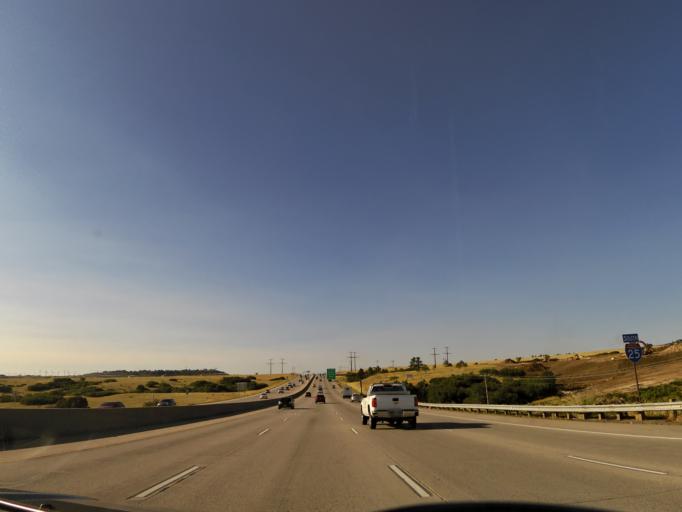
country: US
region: Colorado
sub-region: Park County
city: Castle Pines North
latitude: 39.4658
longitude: -104.8738
